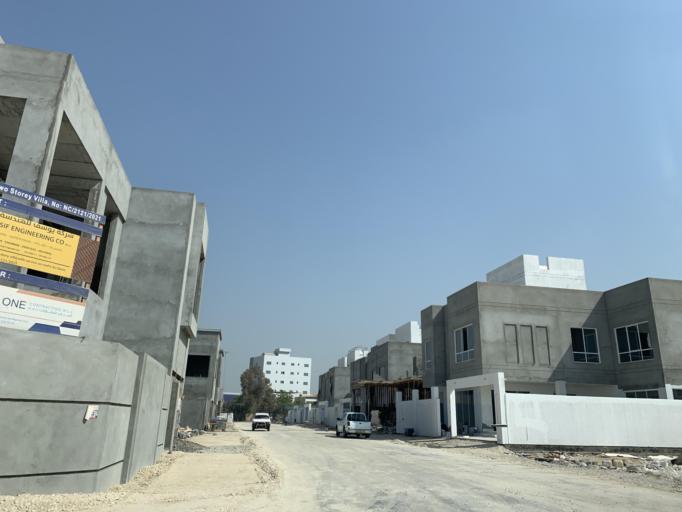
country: BH
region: Northern
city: Madinat `Isa
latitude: 26.1900
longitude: 50.5078
